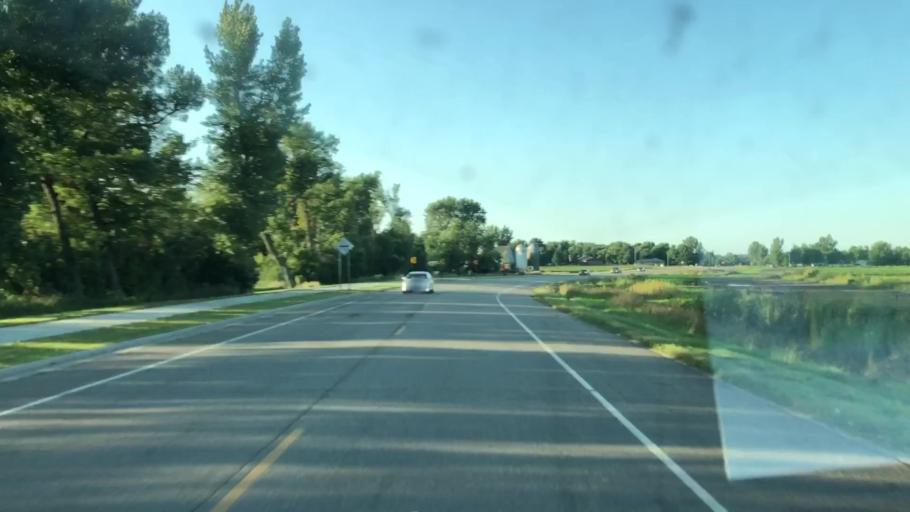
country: US
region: Minnesota
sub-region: Nobles County
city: Worthington
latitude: 43.6212
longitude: -95.6336
